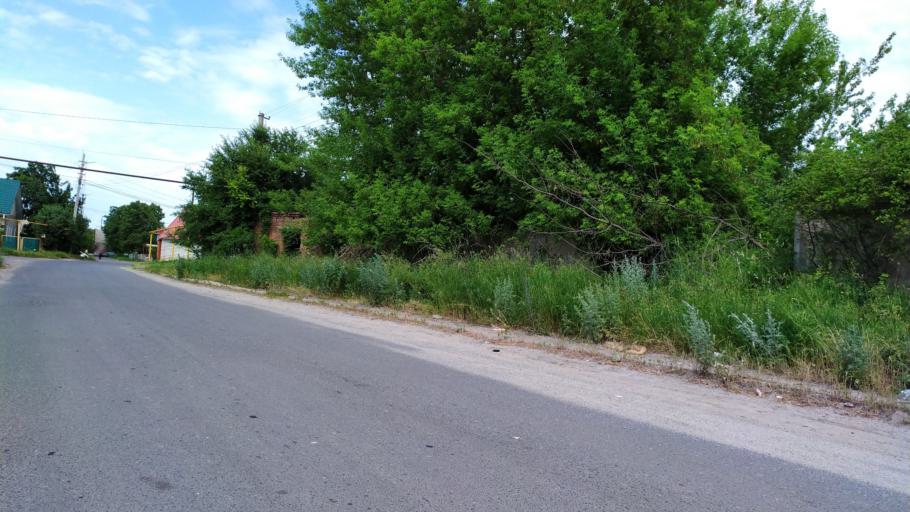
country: RU
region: Kursk
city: Kursk
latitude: 51.6607
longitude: 36.1533
